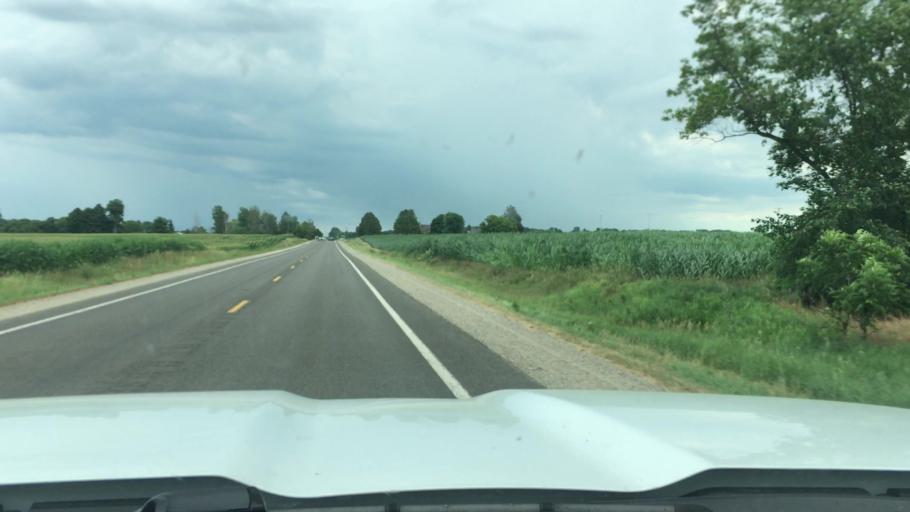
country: US
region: Michigan
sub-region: Montcalm County
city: Carson City
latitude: 43.1775
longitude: -84.9259
